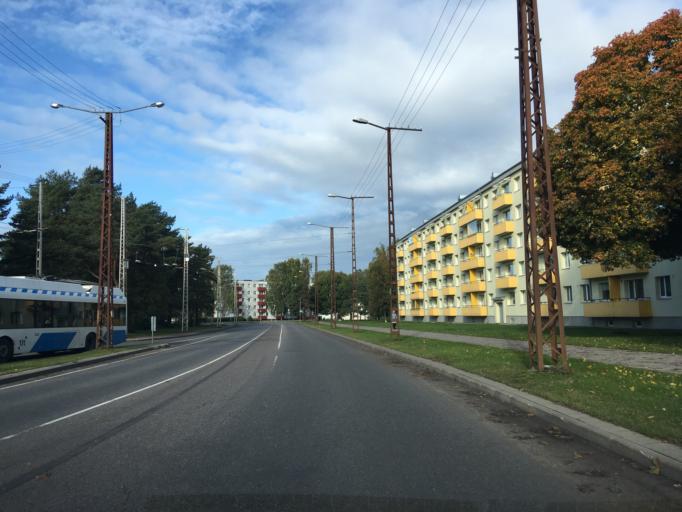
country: EE
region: Harju
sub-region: Tallinna linn
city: Tallinn
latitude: 59.4001
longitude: 24.6800
